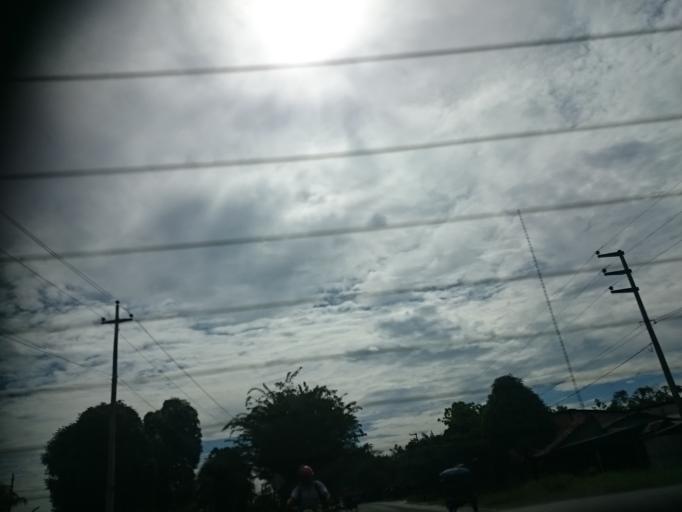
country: PE
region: Loreto
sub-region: Provincia de Maynas
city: Iquitos
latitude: -3.8113
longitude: -73.3172
